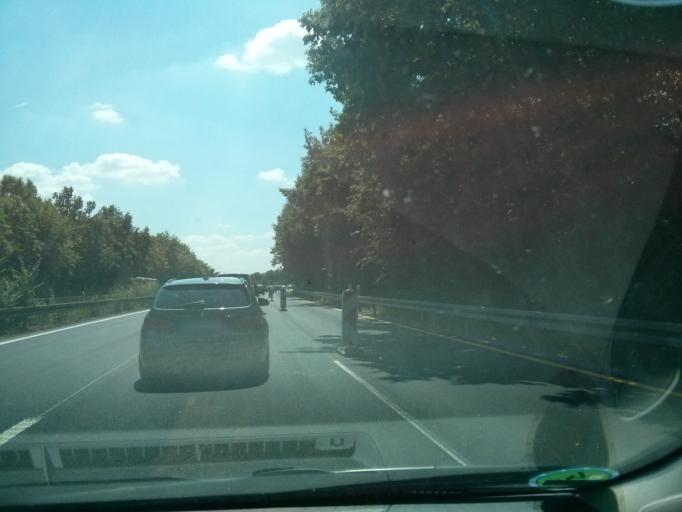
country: DE
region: North Rhine-Westphalia
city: Meckenheim
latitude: 50.6058
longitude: 7.0406
